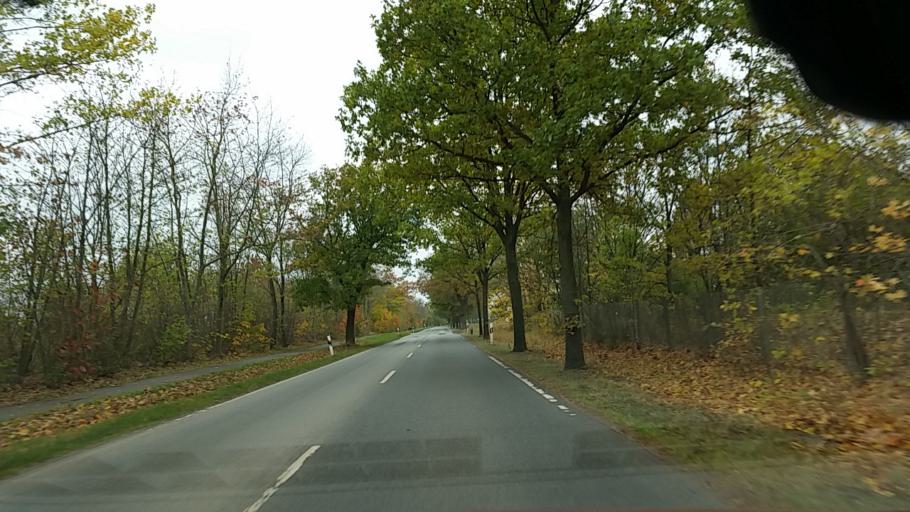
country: DE
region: Lower Saxony
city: Jembke
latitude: 52.4673
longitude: 10.7783
